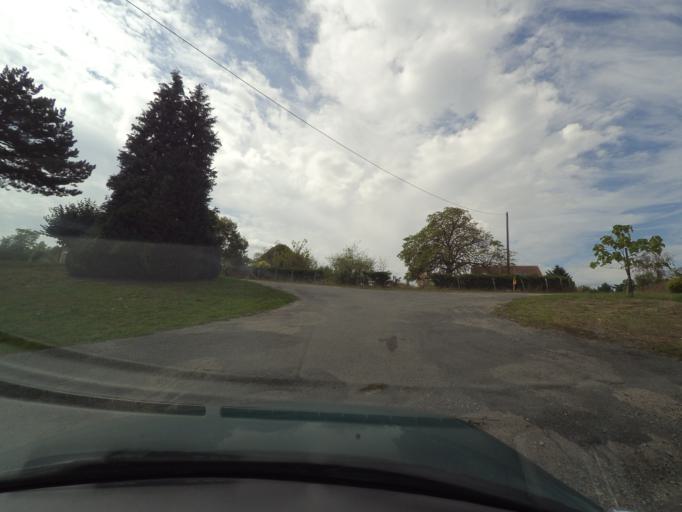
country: FR
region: Limousin
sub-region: Departement de la Haute-Vienne
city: Ladignac-le-Long
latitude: 45.6500
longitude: 1.1164
